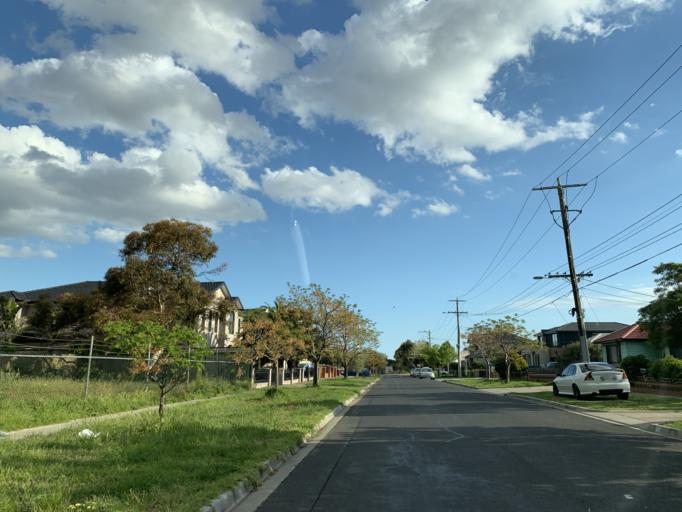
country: AU
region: Victoria
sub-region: Brimbank
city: Albion
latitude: -37.7664
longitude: 144.8448
